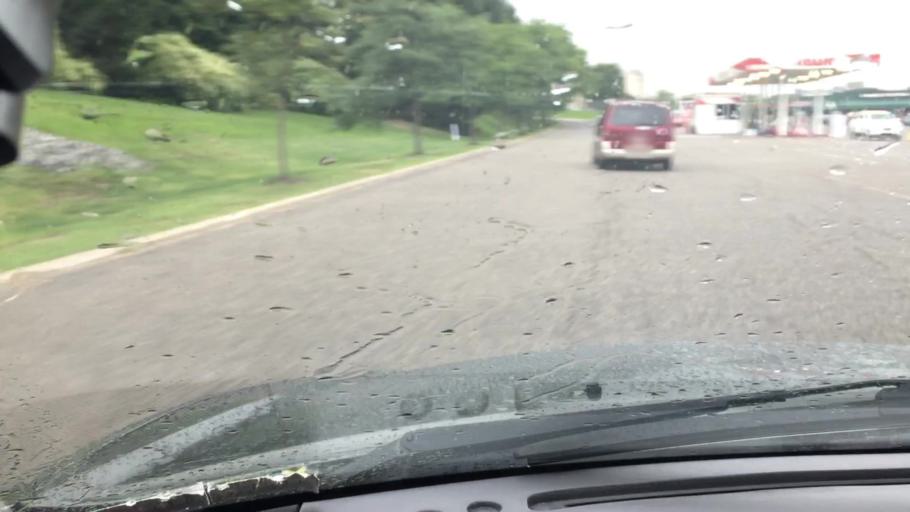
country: US
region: Pennsylvania
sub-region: Luzerne County
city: Hazleton
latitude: 40.9548
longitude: -75.9819
